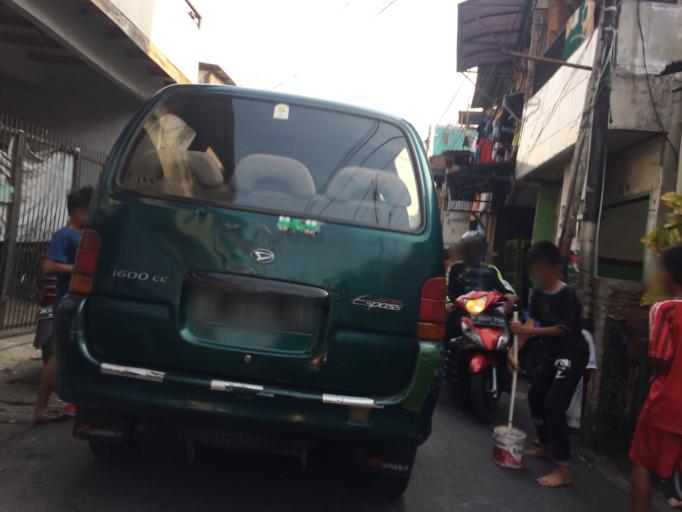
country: ID
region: Jakarta Raya
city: Jakarta
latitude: -6.2087
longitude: 106.8423
